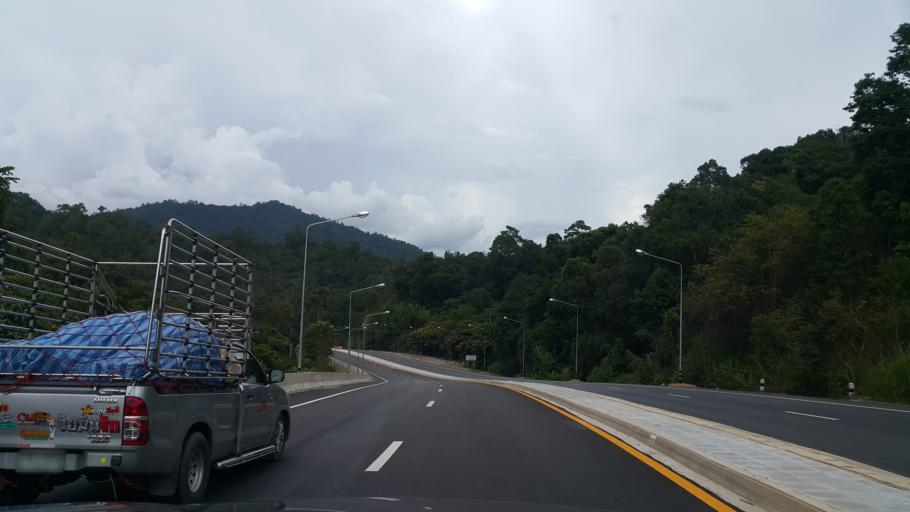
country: TH
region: Lampang
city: Wang Nuea
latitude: 19.0755
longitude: 99.3937
